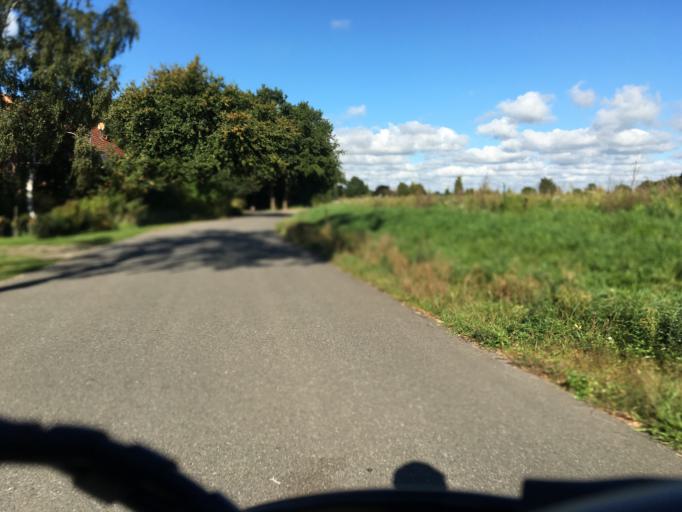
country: DE
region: Lower Saxony
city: Bardowick
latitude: 53.3036
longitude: 10.3801
